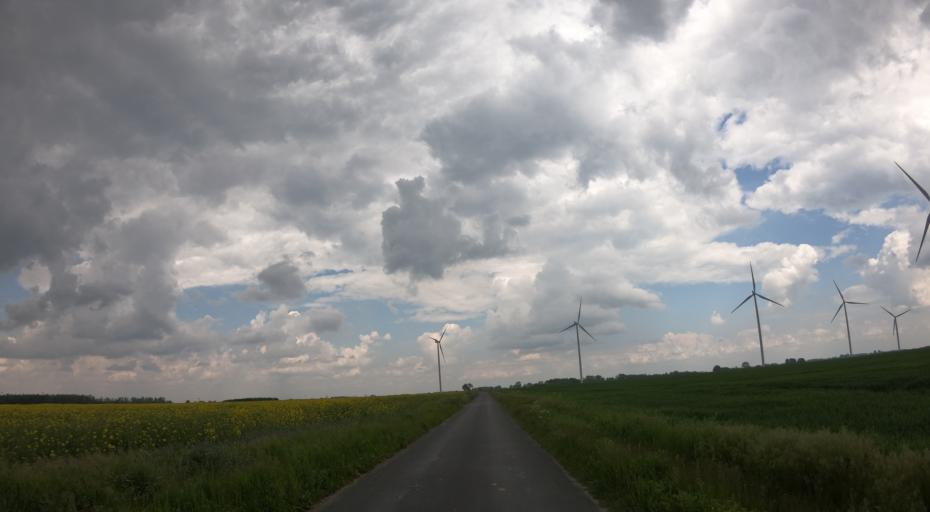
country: PL
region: West Pomeranian Voivodeship
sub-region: Powiat pyrzycki
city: Kozielice
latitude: 53.1450
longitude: 14.7705
